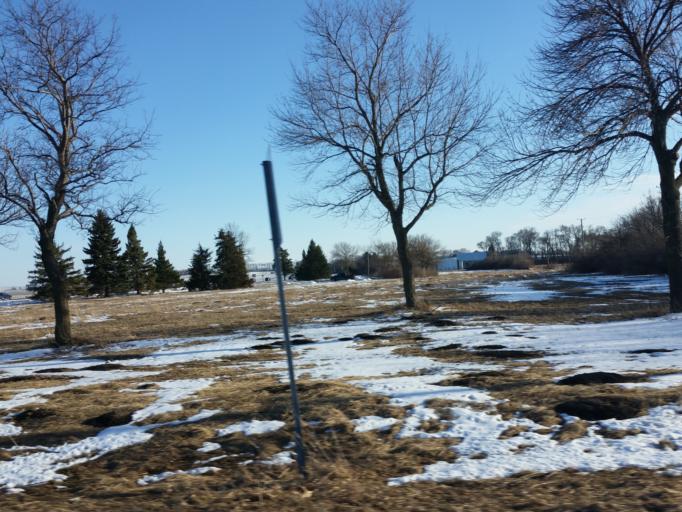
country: US
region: Minnesota
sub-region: Dakota County
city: Rosemount
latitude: 44.7029
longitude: -93.1376
